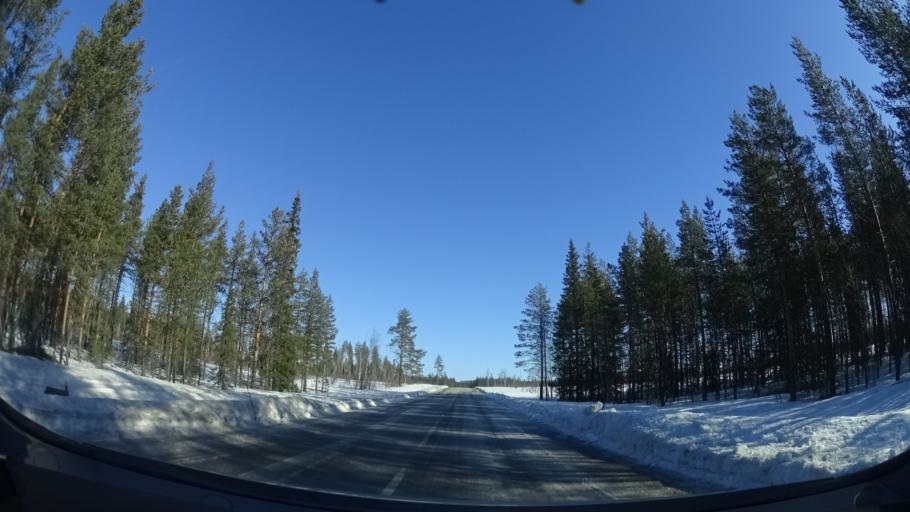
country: SE
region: Vaesterbotten
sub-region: Skelleftea Kommun
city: Langsele
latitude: 65.0664
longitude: 20.0445
